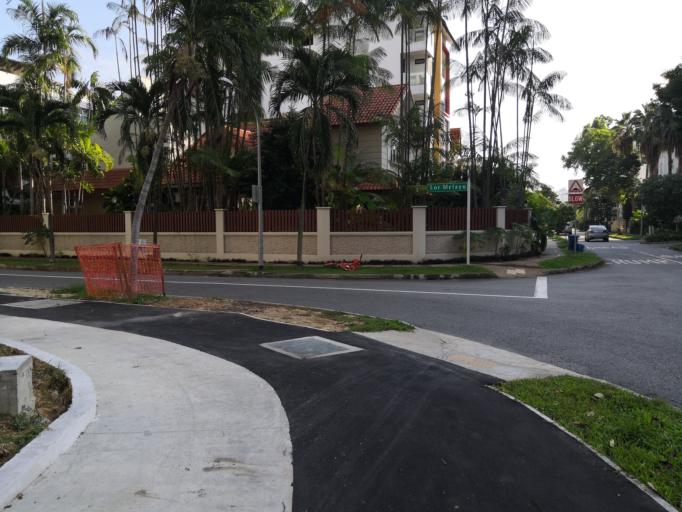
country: SG
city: Singapore
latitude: 1.3261
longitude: 103.9095
